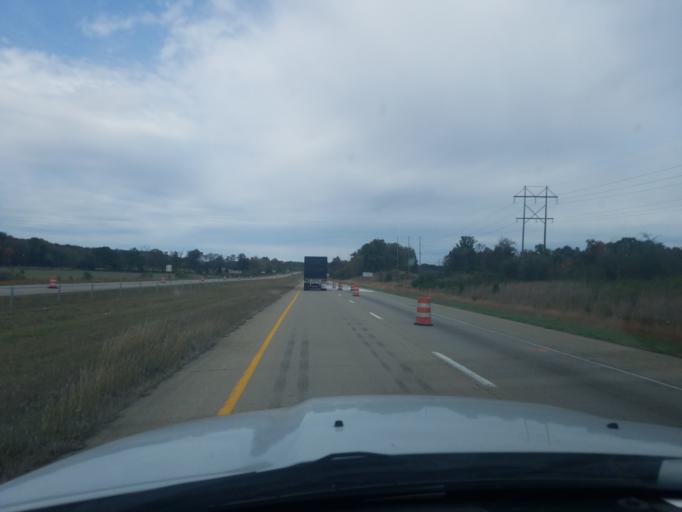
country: US
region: Indiana
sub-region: Gibson County
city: Haubstadt
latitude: 38.1520
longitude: -87.4726
